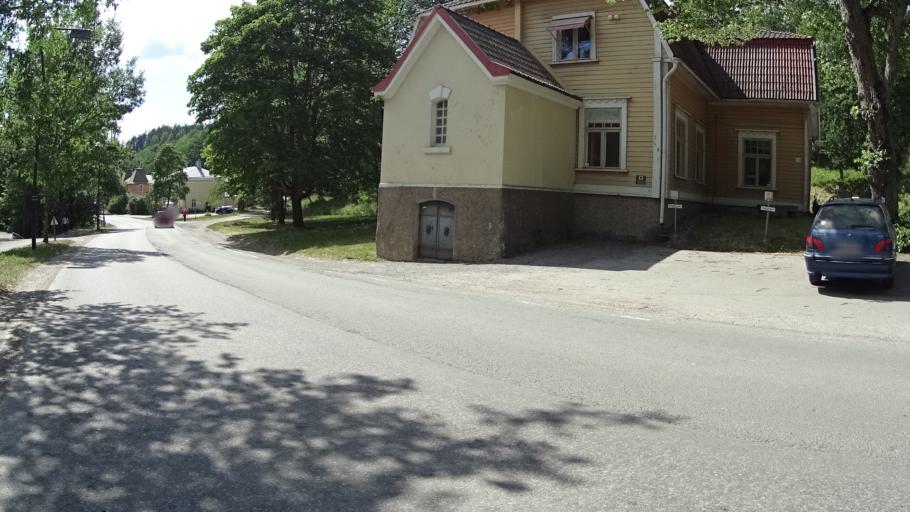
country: FI
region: Uusimaa
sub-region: Raaseporin
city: Pohja
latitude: 60.1281
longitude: 23.5402
